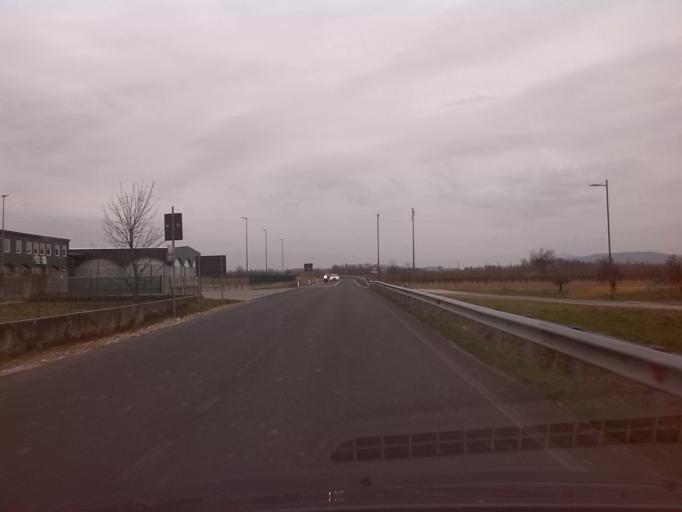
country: IT
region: Friuli Venezia Giulia
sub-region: Provincia di Gorizia
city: Medea
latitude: 45.9176
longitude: 13.4298
